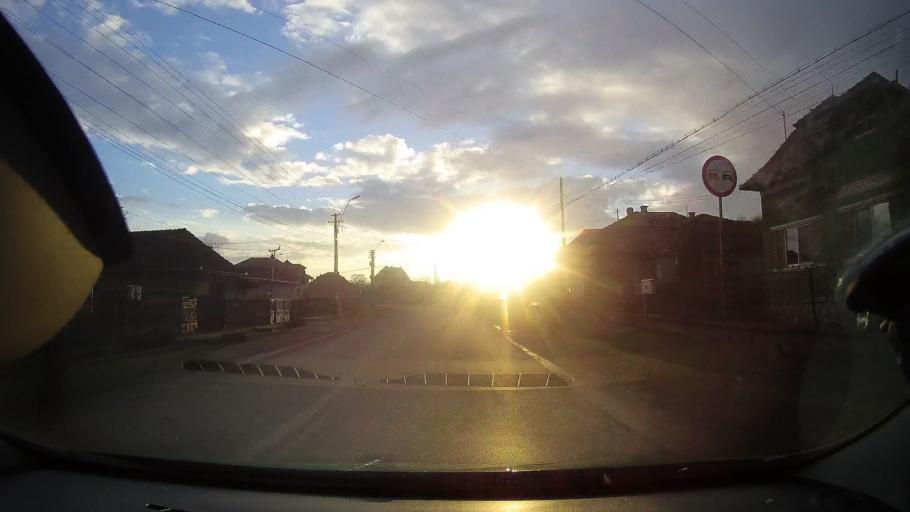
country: RO
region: Alba
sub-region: Oras Ocna Mures
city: Razboieni-Cetate
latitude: 46.4174
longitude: 23.8736
